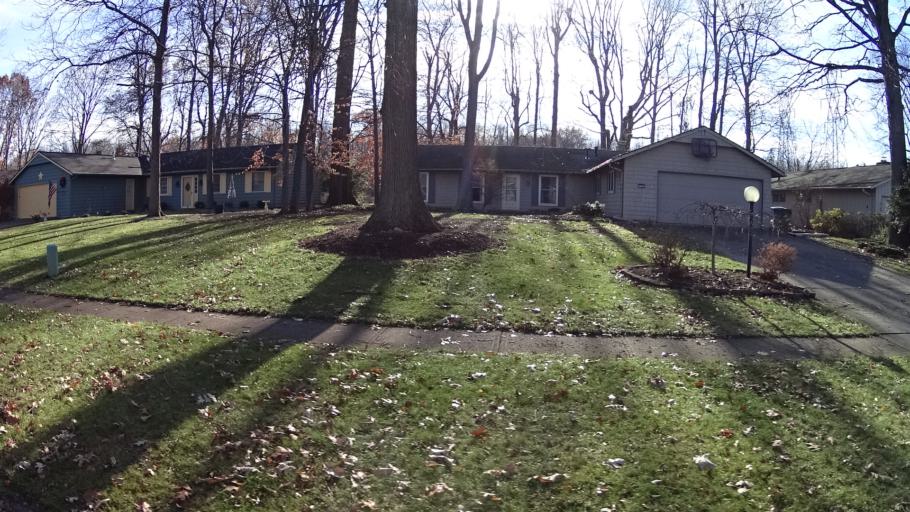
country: US
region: Ohio
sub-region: Lorain County
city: North Ridgeville
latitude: 41.4005
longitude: -81.9809
